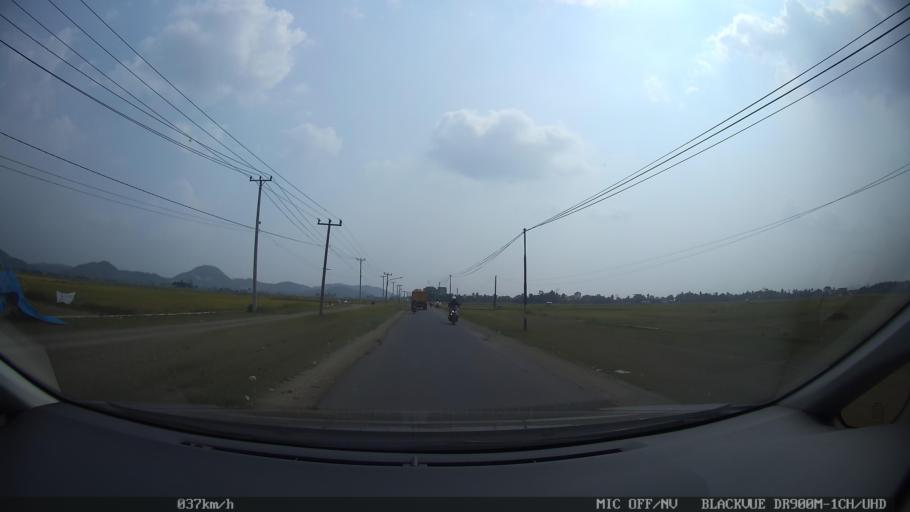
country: ID
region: Lampung
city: Pringsewu
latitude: -5.3554
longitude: 105.0122
